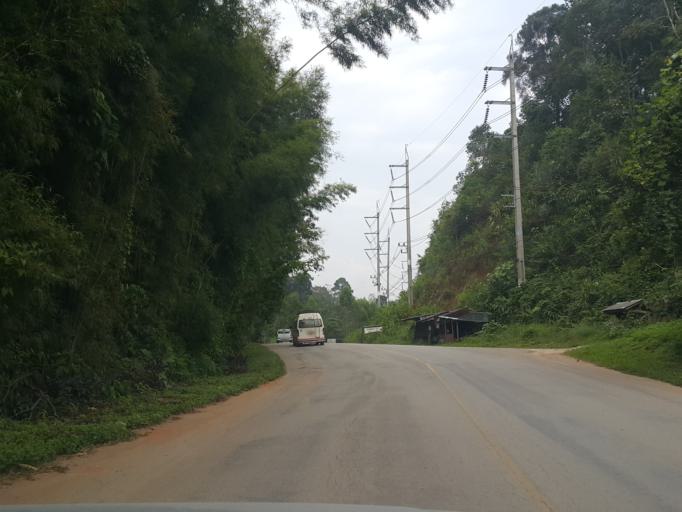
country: TH
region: Chiang Mai
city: Mae Taeng
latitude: 19.1165
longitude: 98.7326
